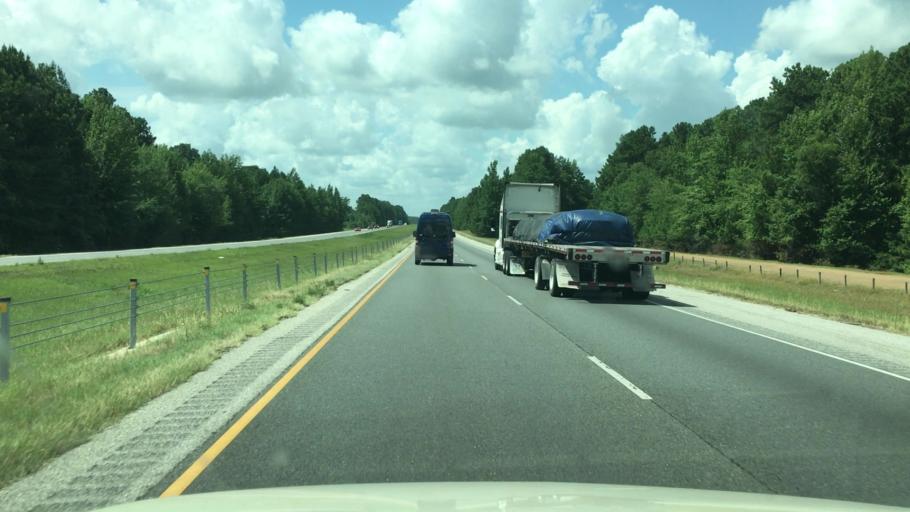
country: US
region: Arkansas
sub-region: Clark County
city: Arkadelphia
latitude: 34.0690
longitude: -93.1229
